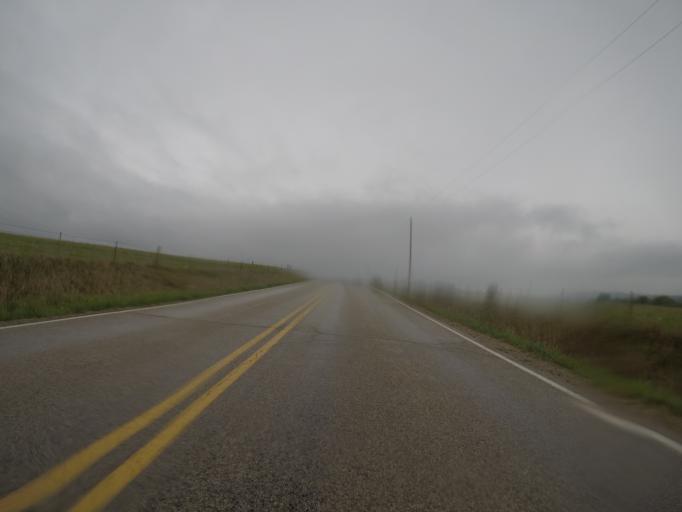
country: US
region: Kansas
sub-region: Pottawatomie County
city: Westmoreland
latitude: 39.4220
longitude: -96.1839
